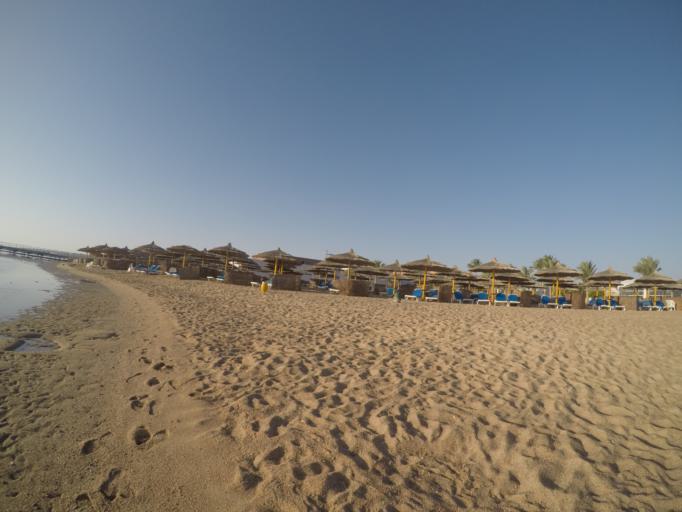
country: EG
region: Red Sea
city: Makadi Bay
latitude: 27.0927
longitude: 33.8526
